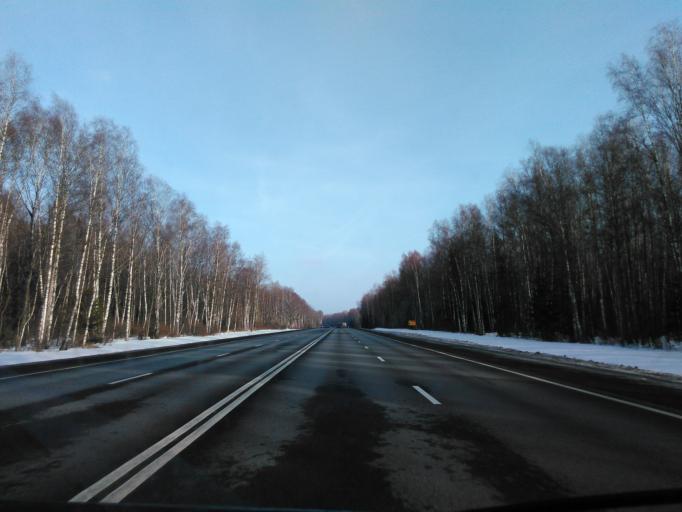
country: RU
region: Smolensk
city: Vyaz'ma
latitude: 55.1880
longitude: 34.0451
